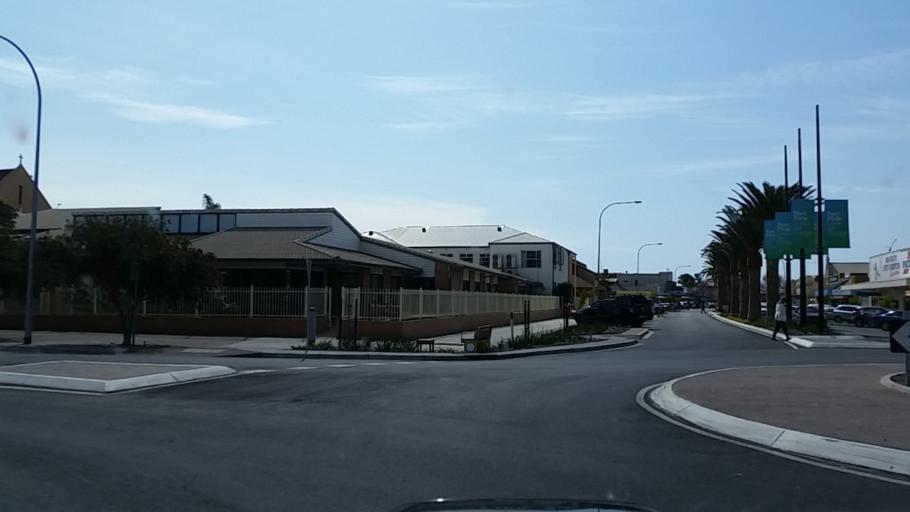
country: AU
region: South Australia
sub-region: Port Pirie City and Dists
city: Port Pirie
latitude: -33.1793
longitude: 138.0093
